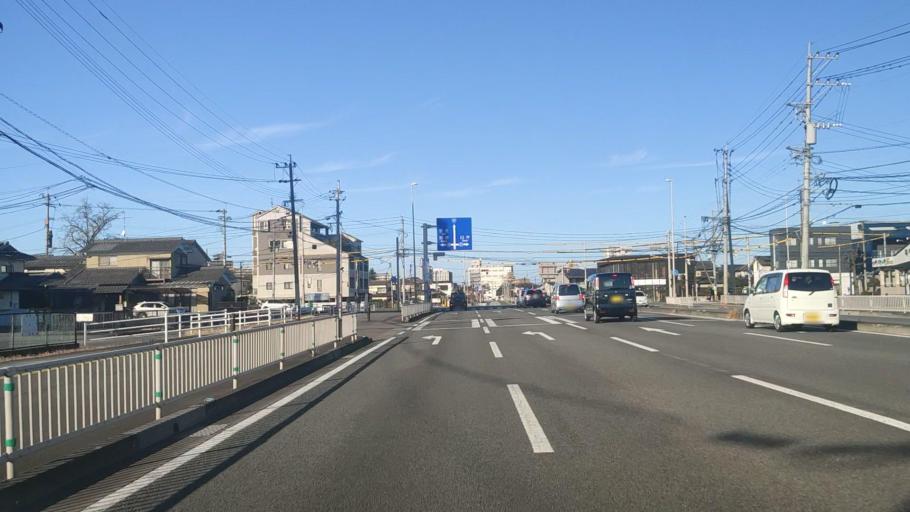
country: JP
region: Oita
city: Oita
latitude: 33.2309
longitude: 131.6189
